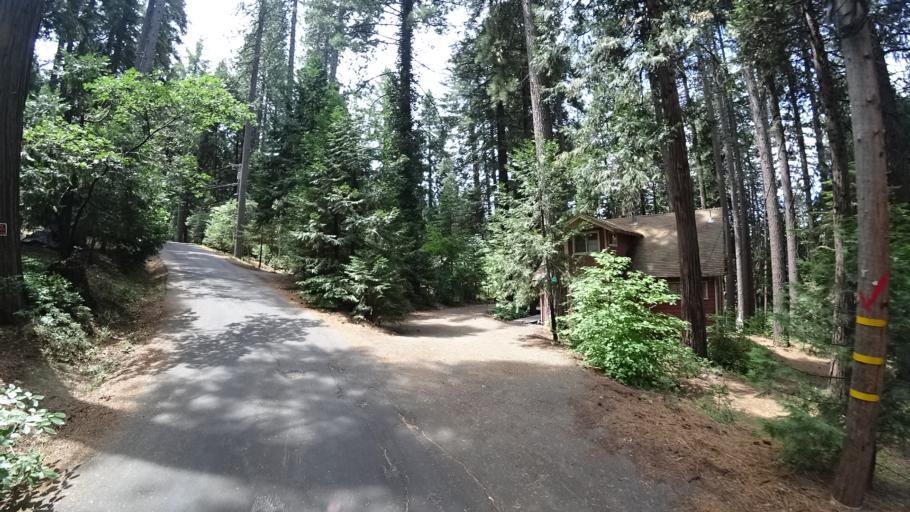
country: US
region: California
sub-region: Calaveras County
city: Arnold
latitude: 38.2534
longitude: -120.3531
